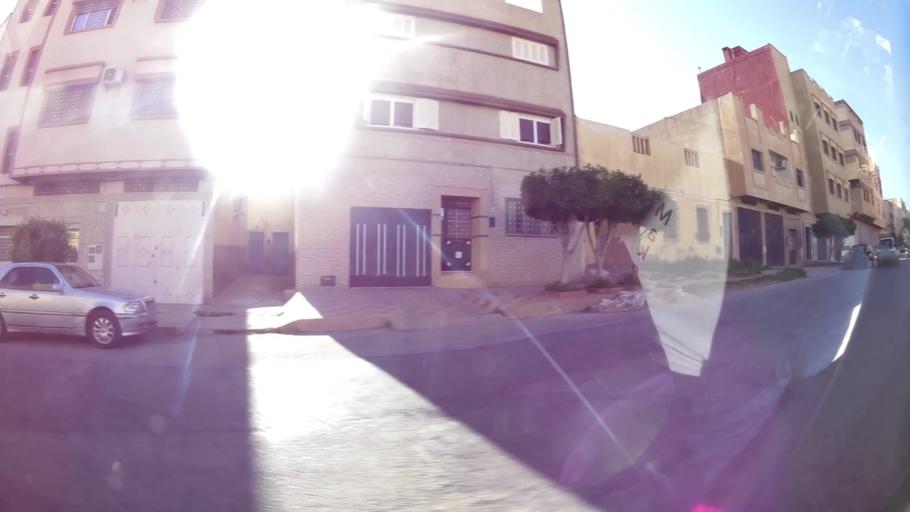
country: MA
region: Oriental
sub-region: Oujda-Angad
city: Oujda
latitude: 34.6885
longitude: -1.9119
